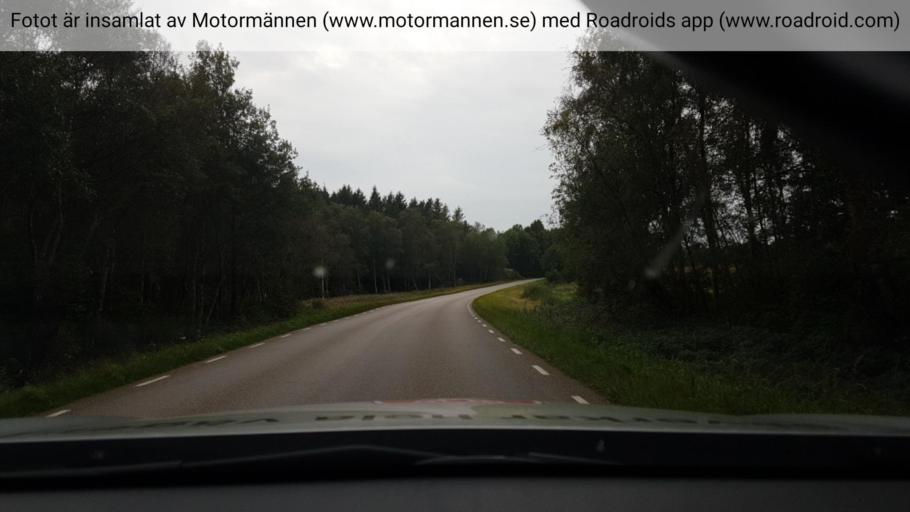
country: SE
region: Vaestra Goetaland
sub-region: Tanums Kommun
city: Grebbestad
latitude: 58.6488
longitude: 11.3037
